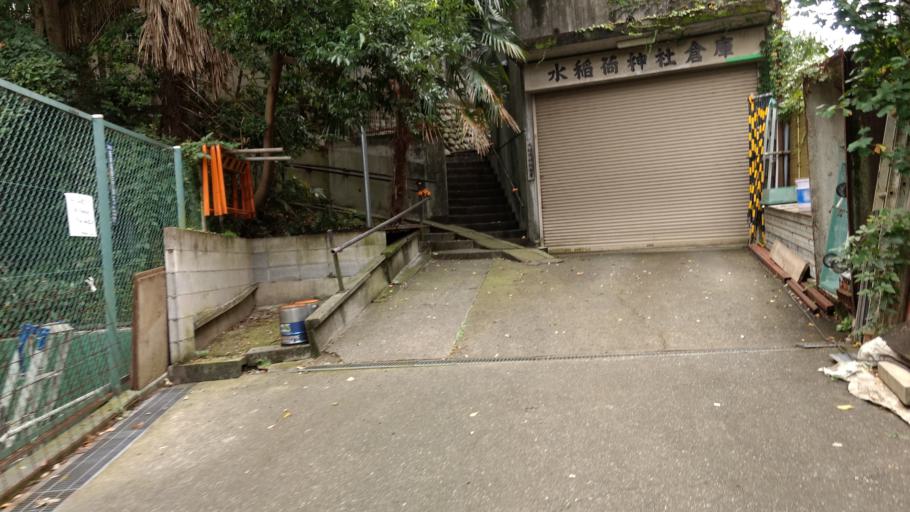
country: JP
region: Tokyo
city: Tokyo
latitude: 35.7119
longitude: 139.7152
